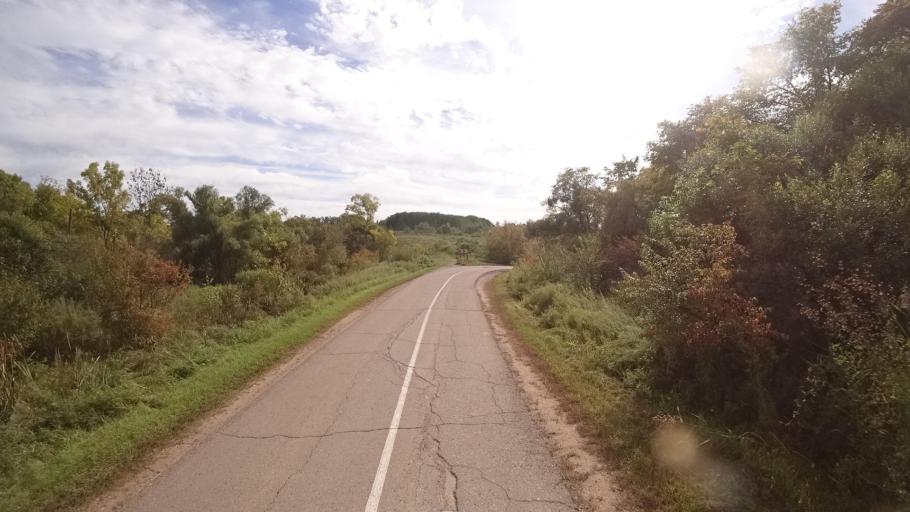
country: RU
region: Primorskiy
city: Dostoyevka
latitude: 44.3314
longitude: 133.4813
